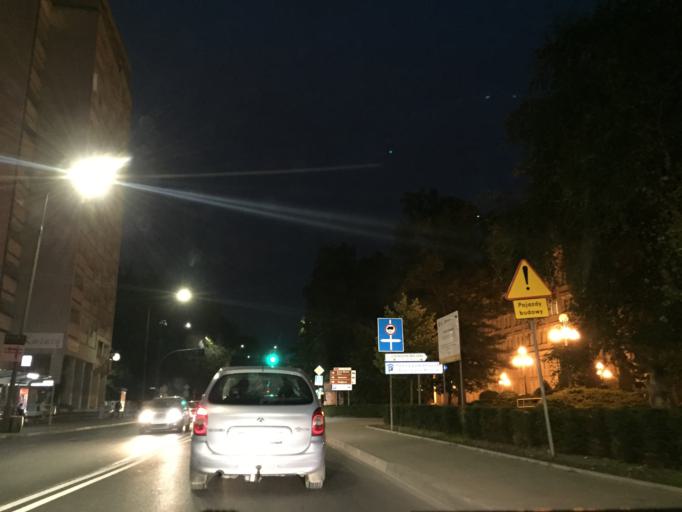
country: PL
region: Lesser Poland Voivodeship
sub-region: Krakow
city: Krakow
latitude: 50.0666
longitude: 19.9217
